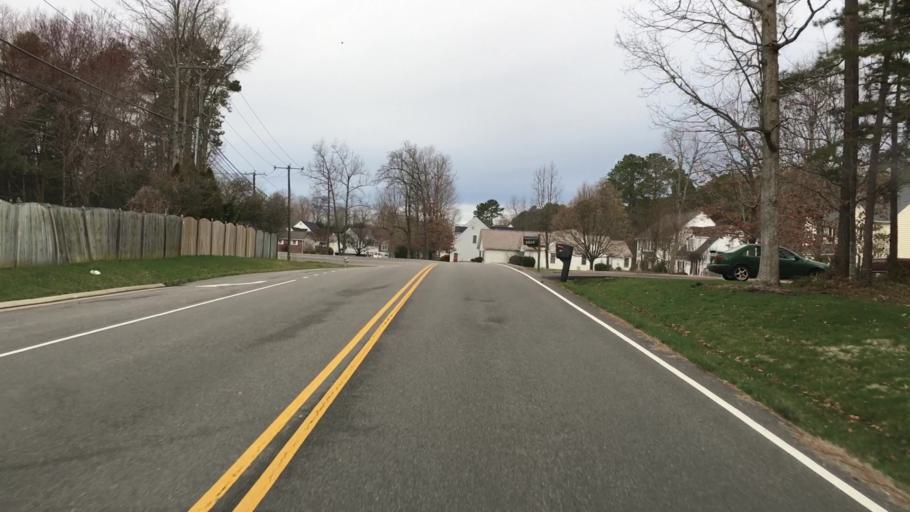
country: US
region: Virginia
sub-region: Henrico County
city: Glen Allen
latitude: 37.6734
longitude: -77.5531
